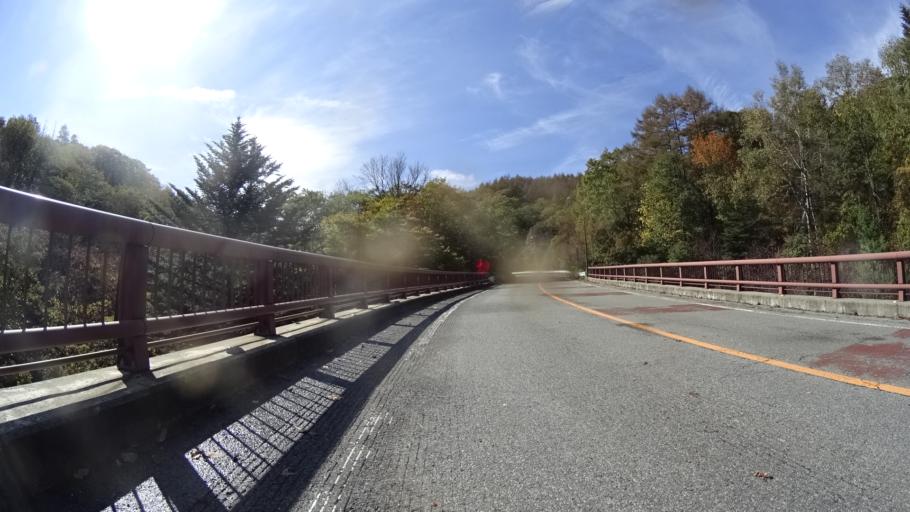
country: JP
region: Yamanashi
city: Enzan
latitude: 35.7817
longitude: 138.8021
